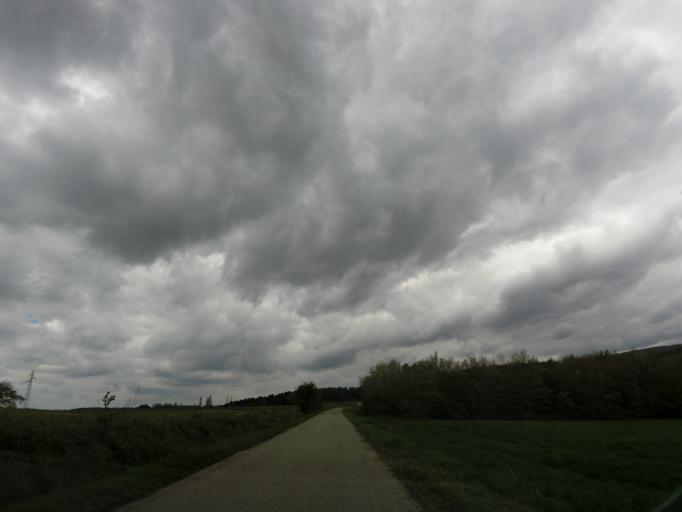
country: FR
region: Languedoc-Roussillon
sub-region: Departement de l'Aude
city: Saint-Martin-Lalande
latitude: 43.3526
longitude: 2.0575
